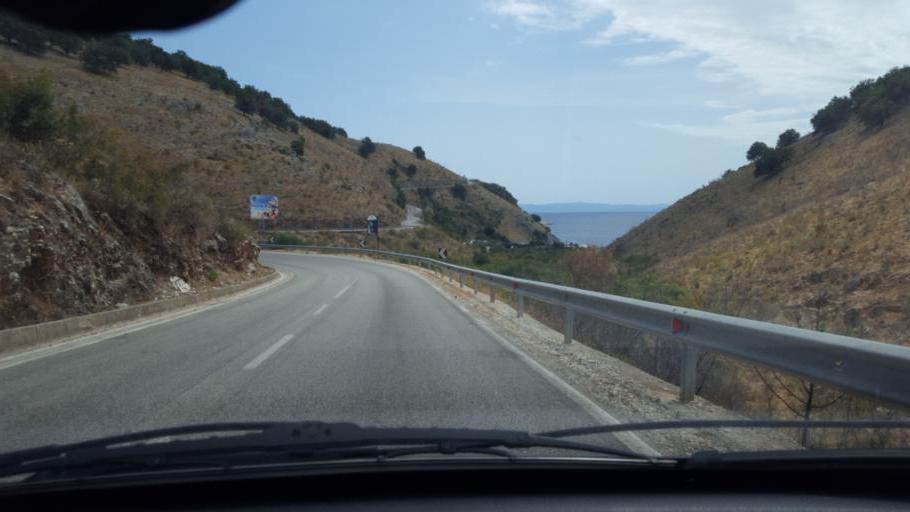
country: AL
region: Vlore
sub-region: Rrethi i Vlores
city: Himare
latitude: 40.0861
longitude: 19.7669
